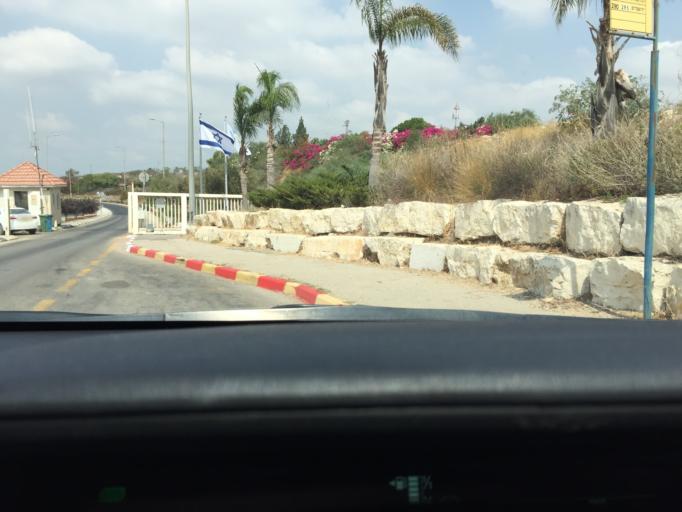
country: PS
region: West Bank
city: Azun Atme
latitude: 32.1135
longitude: 35.0340
